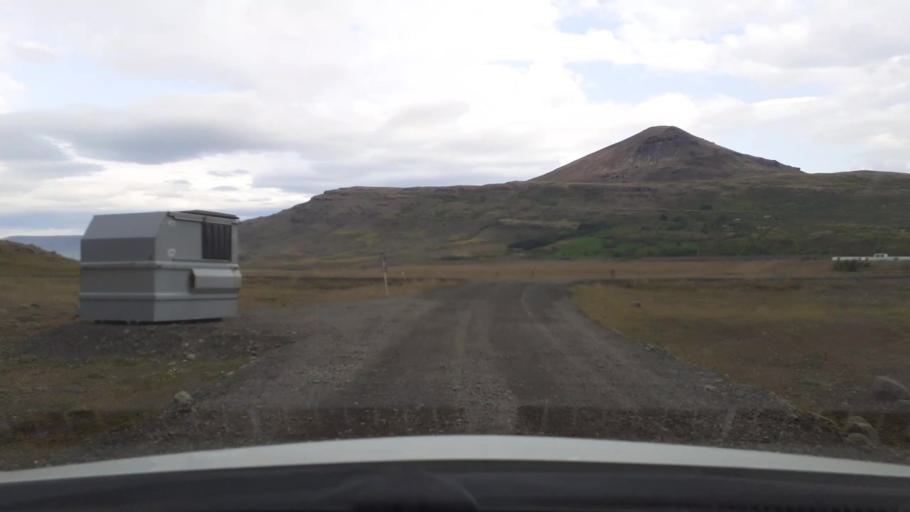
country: IS
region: Capital Region
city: Mosfellsbaer
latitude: 64.2905
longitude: -21.4611
